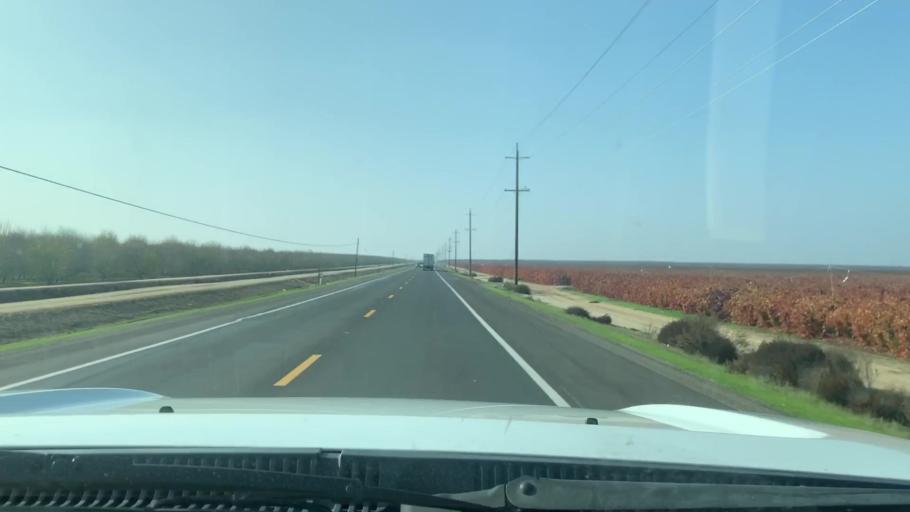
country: US
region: California
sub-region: Kern County
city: Wasco
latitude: 35.6018
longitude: -119.2641
